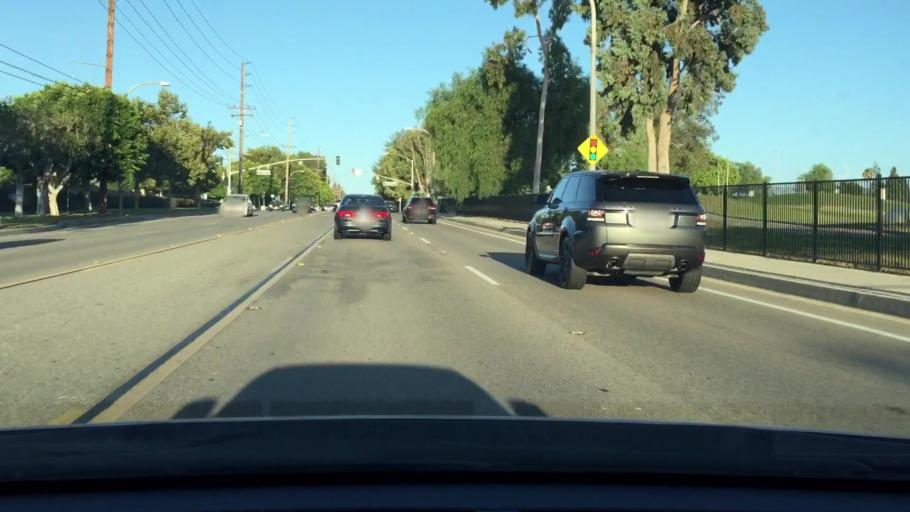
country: US
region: California
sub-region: Orange County
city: Brea
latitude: 33.9182
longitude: -117.8721
